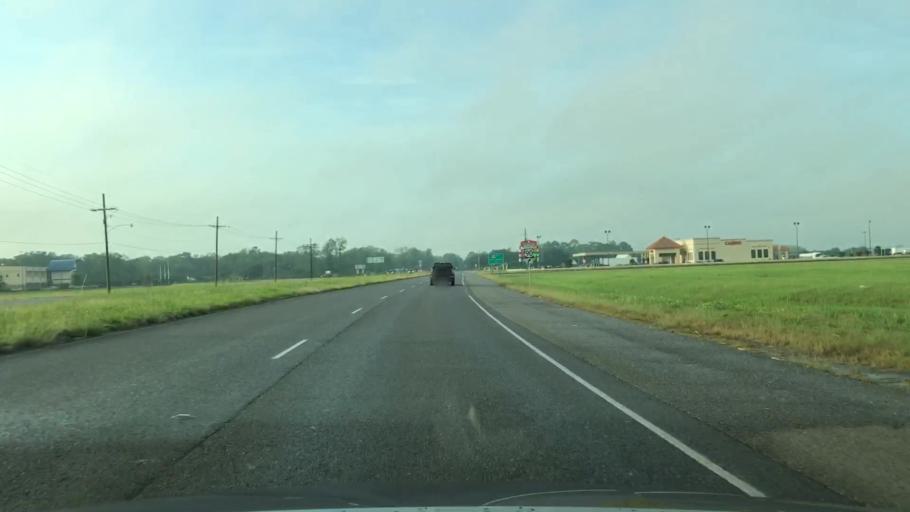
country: US
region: Louisiana
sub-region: Terrebonne Parish
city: Gray
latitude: 29.6813
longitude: -90.8120
